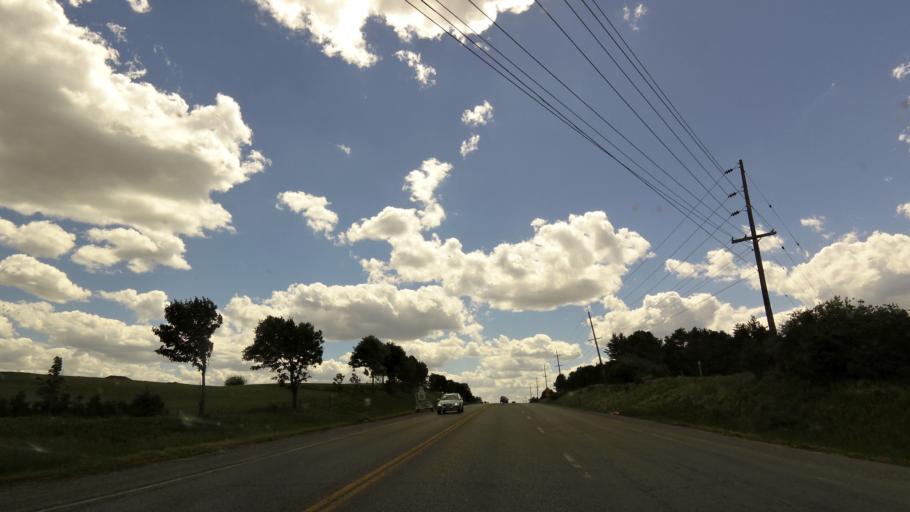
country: CA
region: Ontario
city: Uxbridge
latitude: 44.0327
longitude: -79.2043
